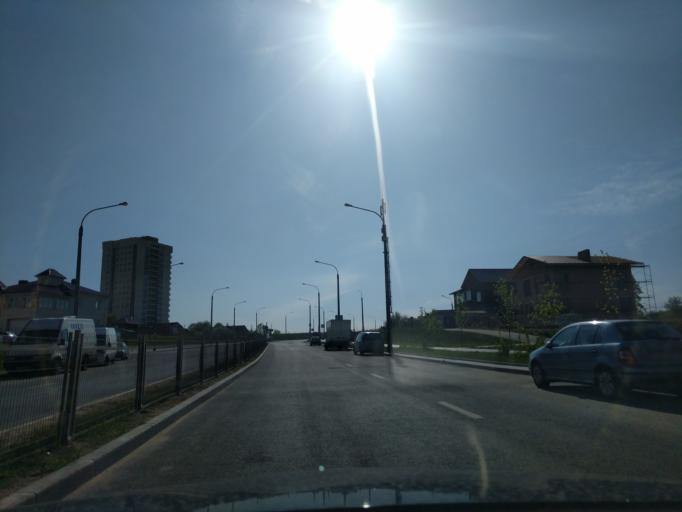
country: BY
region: Minsk
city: Novoye Medvezhino
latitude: 53.8770
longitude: 27.4440
